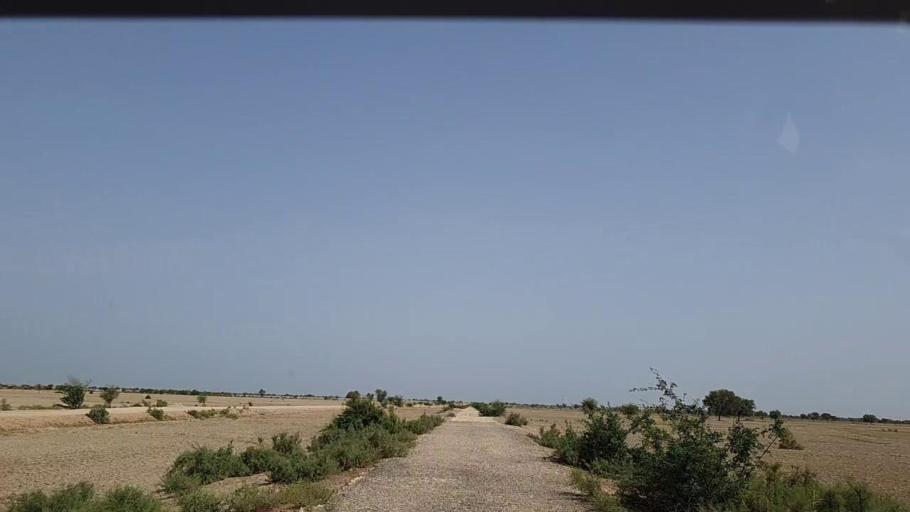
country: PK
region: Sindh
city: Johi
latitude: 26.7487
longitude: 67.6723
